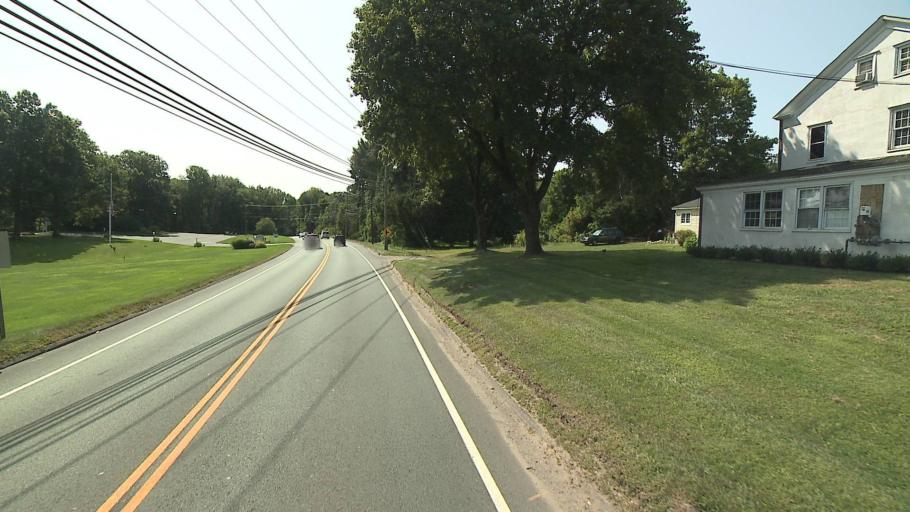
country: US
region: Connecticut
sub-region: Fairfield County
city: Newtown
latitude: 41.3829
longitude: -73.2847
